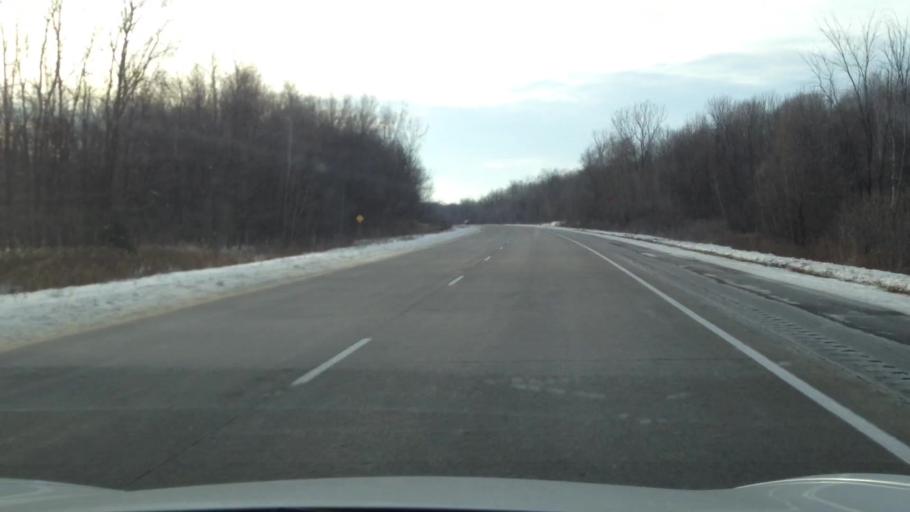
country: CA
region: Ontario
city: Hawkesbury
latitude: 45.4486
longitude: -74.7185
